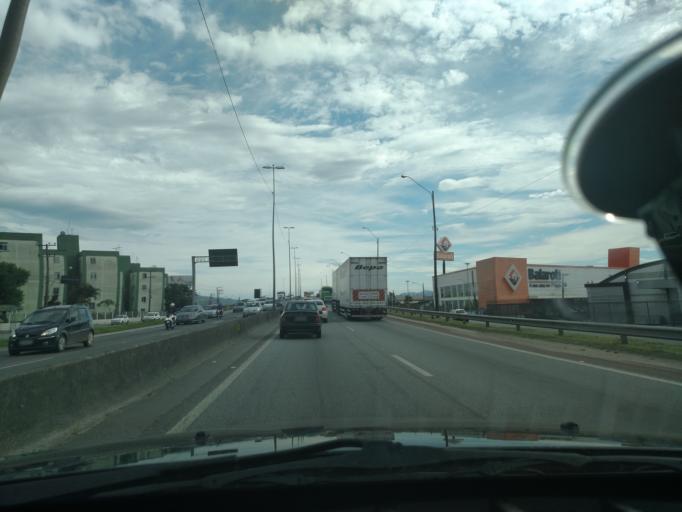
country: BR
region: Santa Catarina
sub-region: Sao Jose
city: Campinas
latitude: -27.5687
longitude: -48.6139
